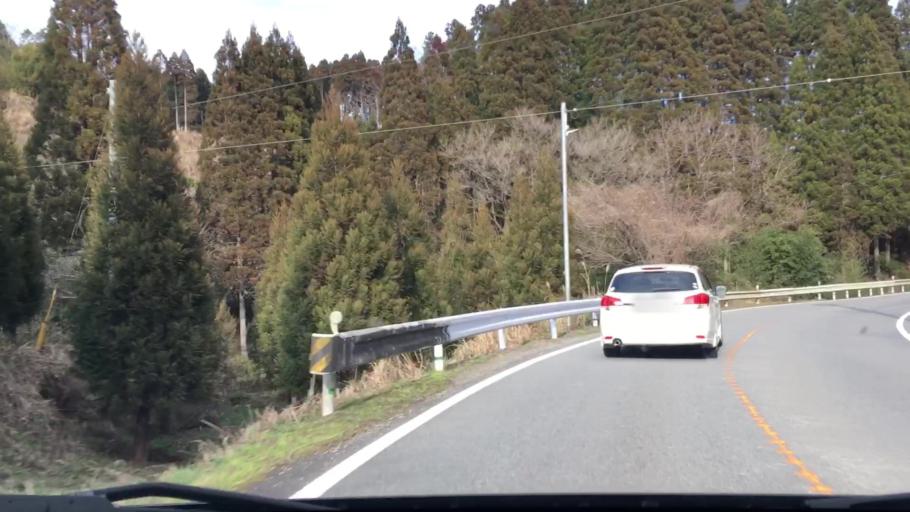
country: JP
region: Miyazaki
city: Nichinan
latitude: 31.7218
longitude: 131.3265
